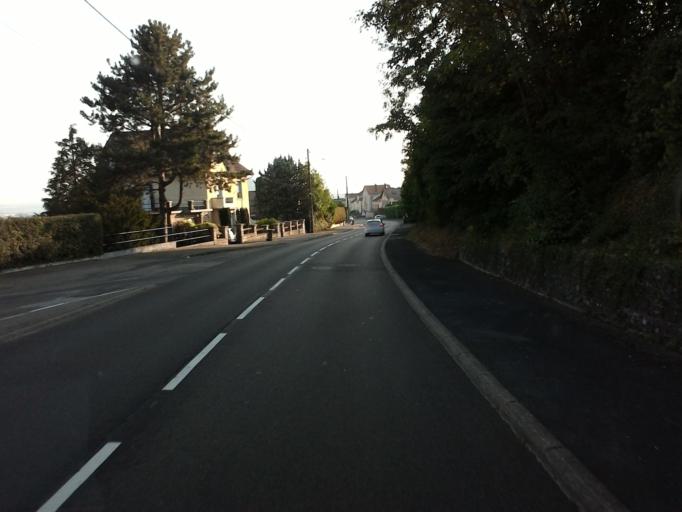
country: FR
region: Franche-Comte
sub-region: Departement de la Haute-Saone
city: Echenoz-la-Meline
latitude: 47.6039
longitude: 6.1416
